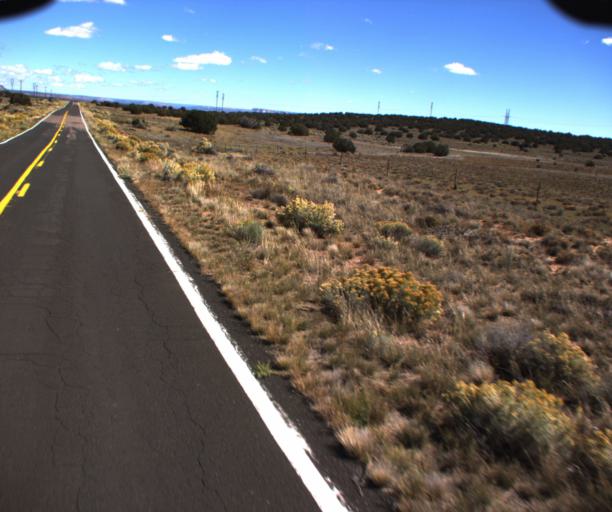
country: US
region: New Mexico
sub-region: McKinley County
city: Zuni Pueblo
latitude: 35.0153
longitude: -109.0572
